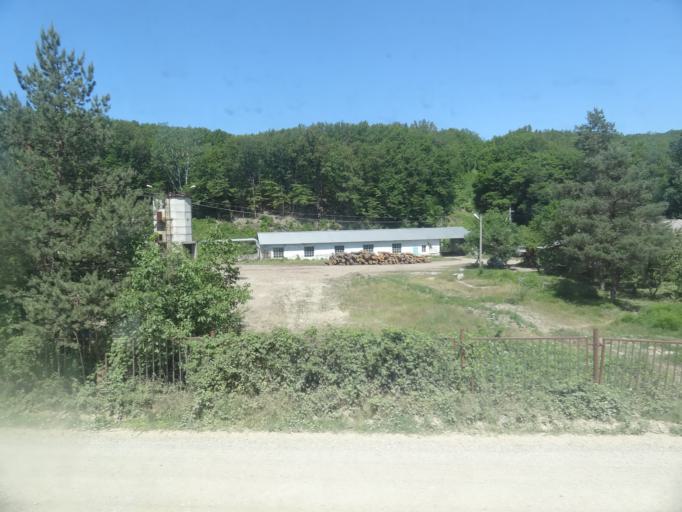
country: RU
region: Krasnodarskiy
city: Goryachiy Klyuch
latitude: 44.6351
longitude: 39.0997
